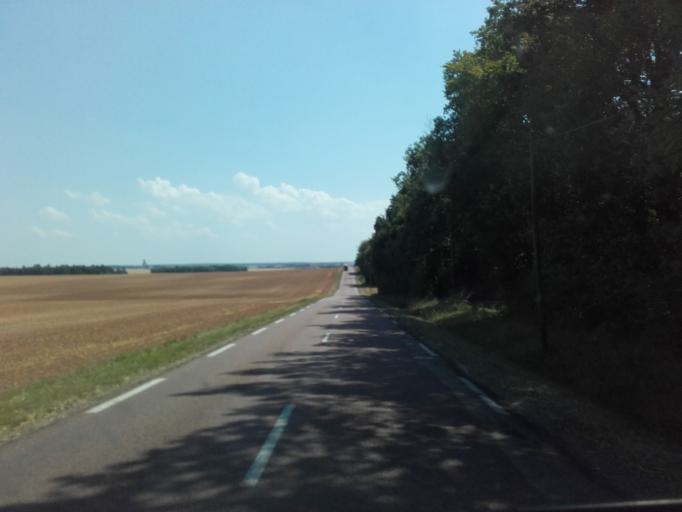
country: FR
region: Bourgogne
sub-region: Departement de l'Yonne
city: Joux-la-Ville
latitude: 47.6992
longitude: 3.8603
